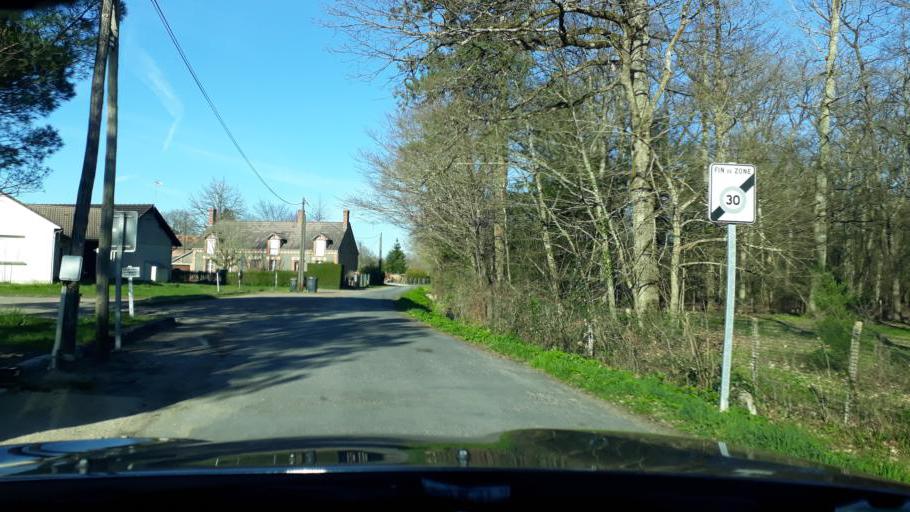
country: FR
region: Centre
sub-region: Departement du Loiret
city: Ligny-le-Ribault
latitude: 47.6868
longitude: 1.7842
